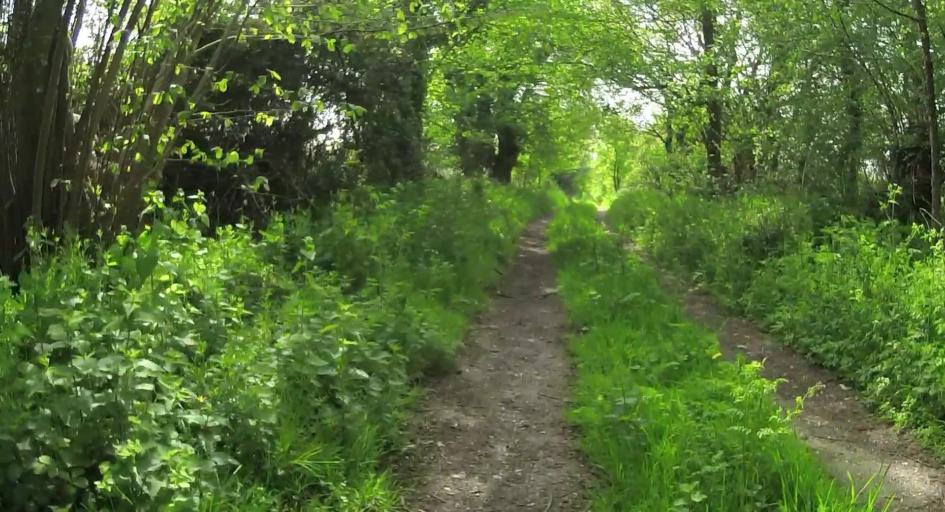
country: GB
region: England
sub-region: Hampshire
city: Andover
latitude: 51.1658
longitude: -1.4109
